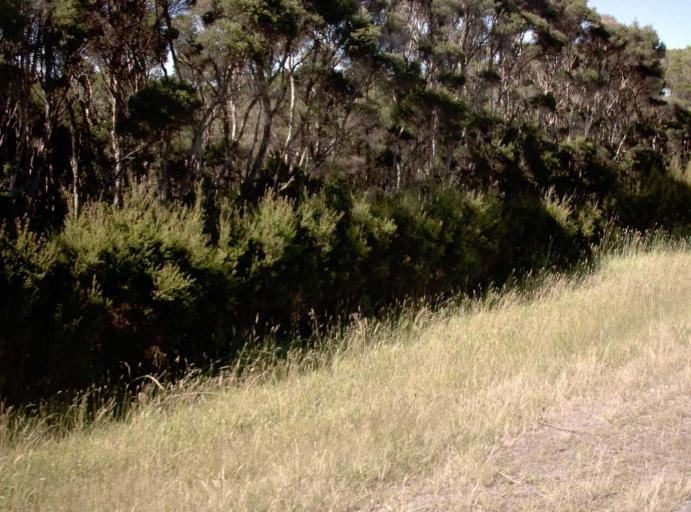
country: AU
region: Victoria
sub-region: Latrobe
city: Traralgon
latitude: -38.6312
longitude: 146.5927
